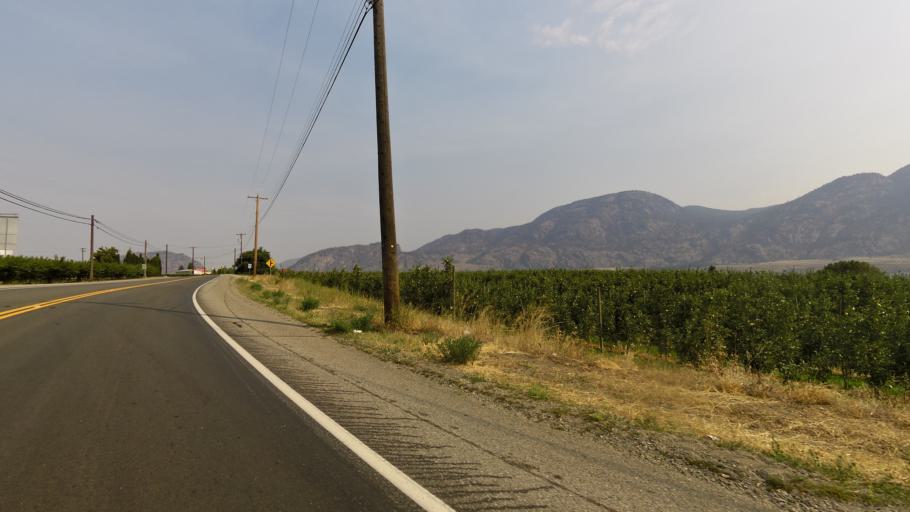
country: CA
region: British Columbia
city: Osoyoos
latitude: 49.0480
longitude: -119.4980
